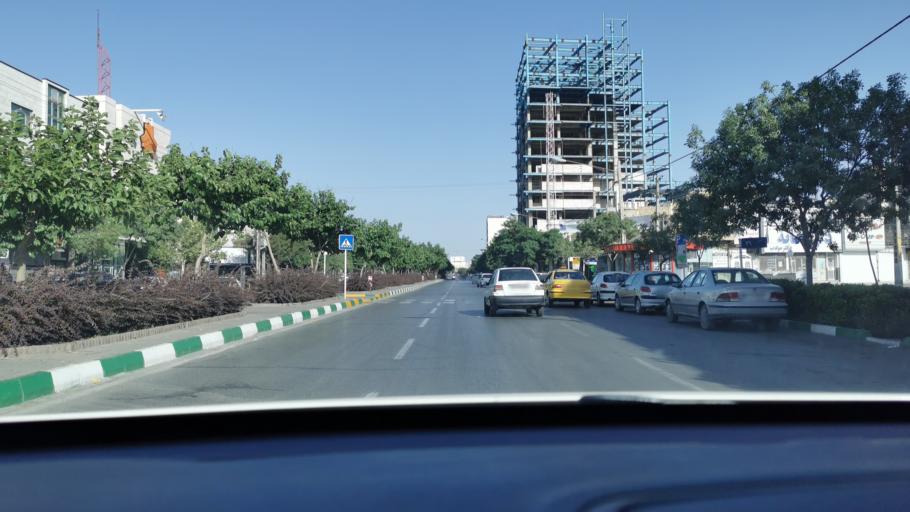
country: IR
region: Razavi Khorasan
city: Mashhad
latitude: 36.3319
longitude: 59.5176
